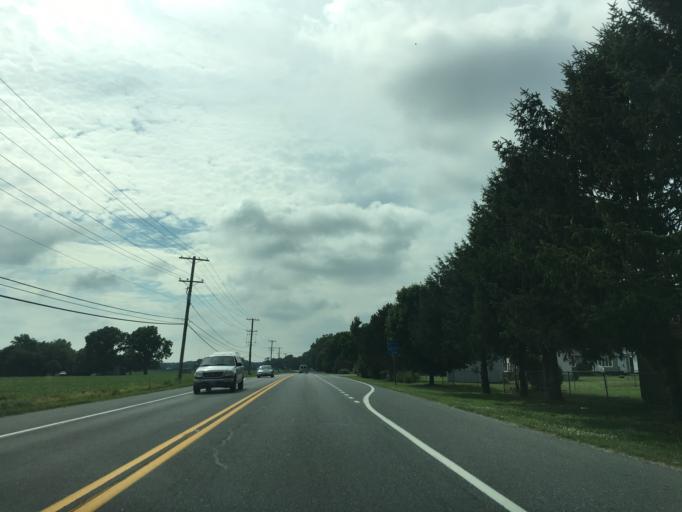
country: US
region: Delaware
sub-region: Sussex County
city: Long Neck
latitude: 38.5556
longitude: -75.1575
